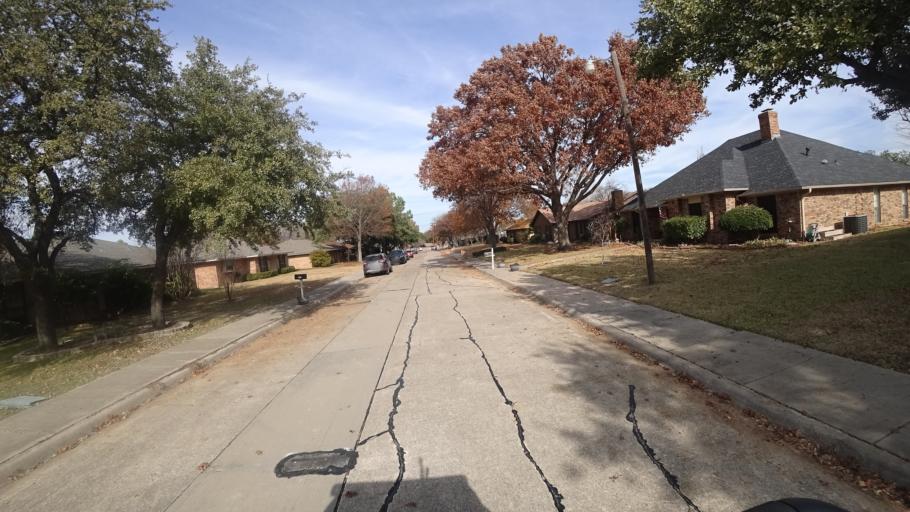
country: US
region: Texas
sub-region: Denton County
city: Highland Village
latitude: 33.0733
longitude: -97.0414
